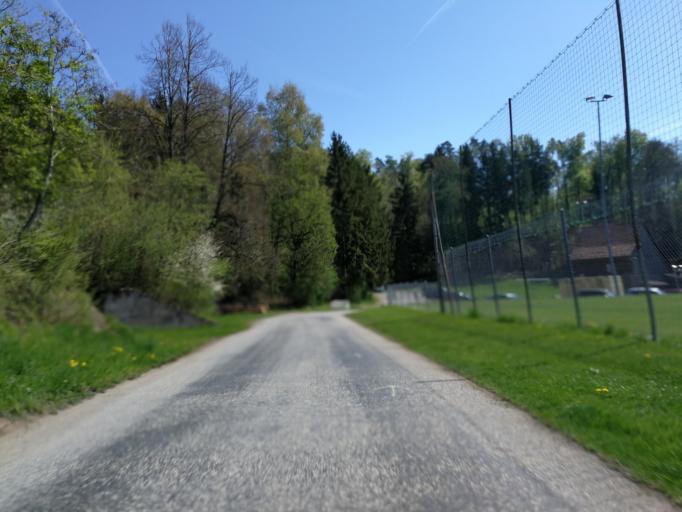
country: CH
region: Zurich
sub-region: Bezirk Meilen
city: Oetwil am See
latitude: 47.2599
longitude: 8.7130
